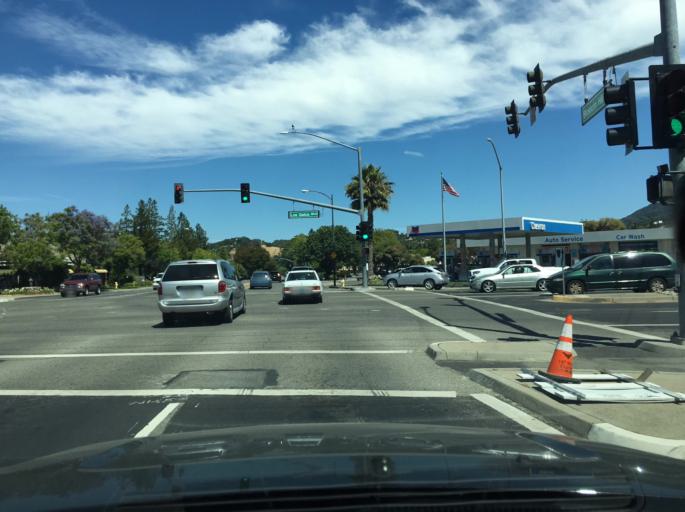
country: US
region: California
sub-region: Santa Clara County
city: Los Gatos
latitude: 37.2357
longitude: -121.9635
